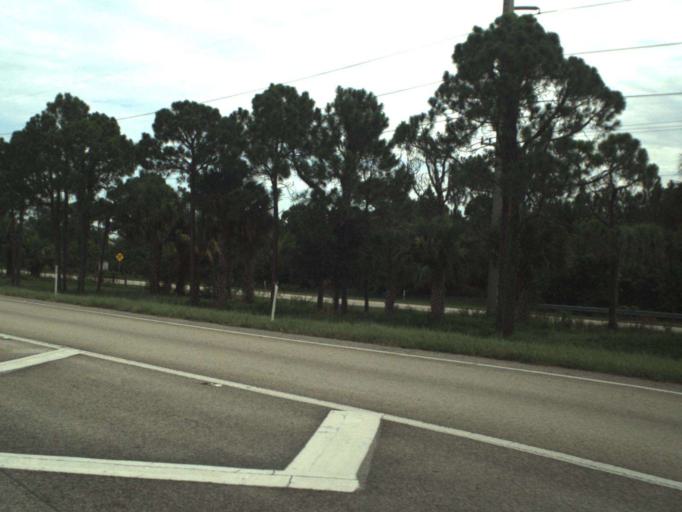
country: US
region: Florida
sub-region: Martin County
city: Palm City
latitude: 27.1135
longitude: -80.2633
